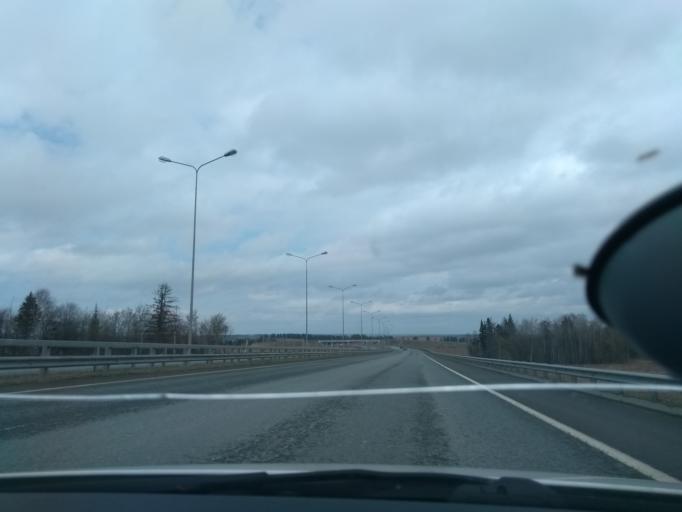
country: RU
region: Perm
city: Zvezdnyy
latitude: 57.7754
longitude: 56.3385
